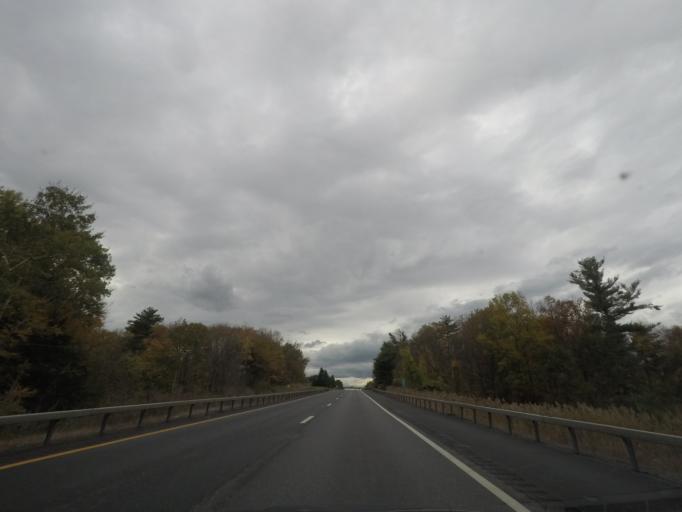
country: US
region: New York
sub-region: Rensselaer County
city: Castleton-on-Hudson
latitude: 42.4987
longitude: -73.7347
